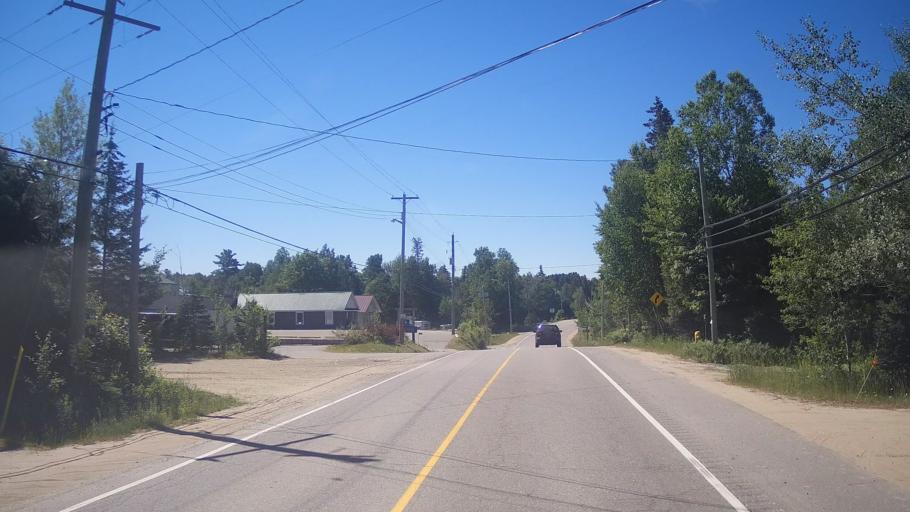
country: CA
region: Ontario
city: Huntsville
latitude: 45.3528
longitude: -79.2020
